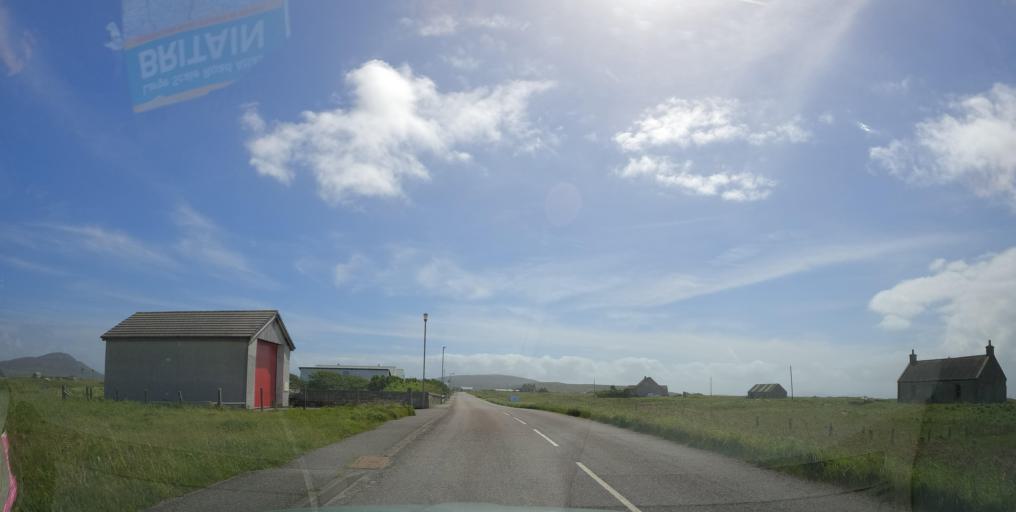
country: GB
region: Scotland
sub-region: Eilean Siar
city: Isle of South Uist
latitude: 57.1664
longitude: -7.3724
